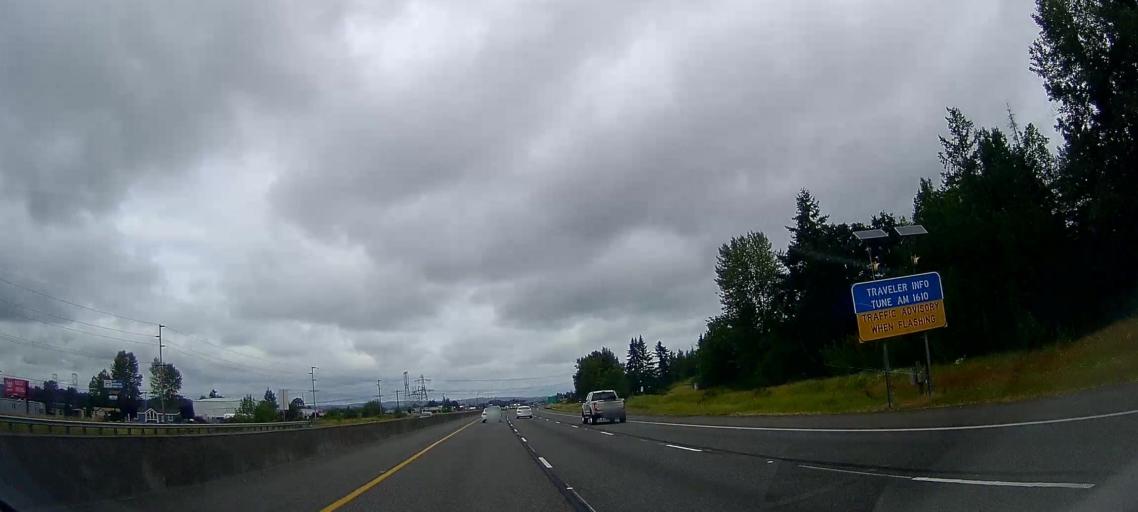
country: US
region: Washington
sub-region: Lewis County
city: Napavine
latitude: 46.6173
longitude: -122.9221
